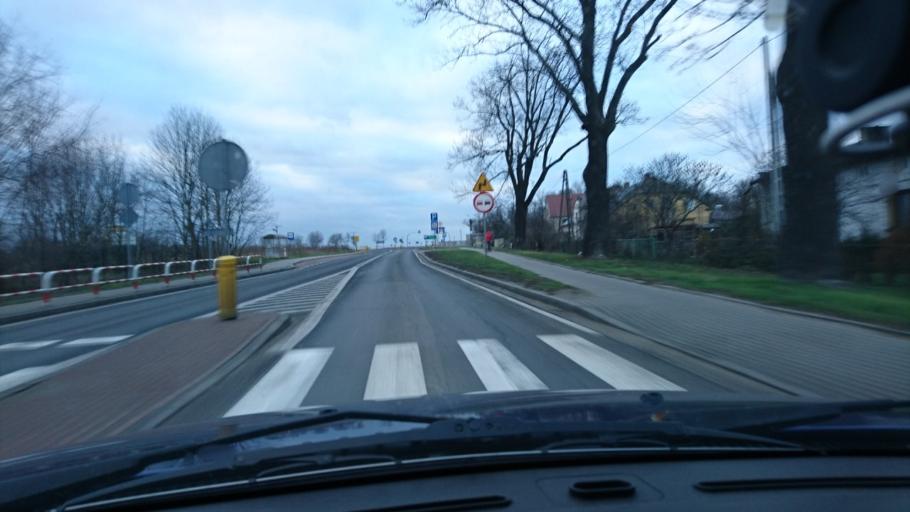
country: PL
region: Greater Poland Voivodeship
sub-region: Powiat kepinski
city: Slupia pod Kepnem
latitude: 51.2388
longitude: 18.0407
